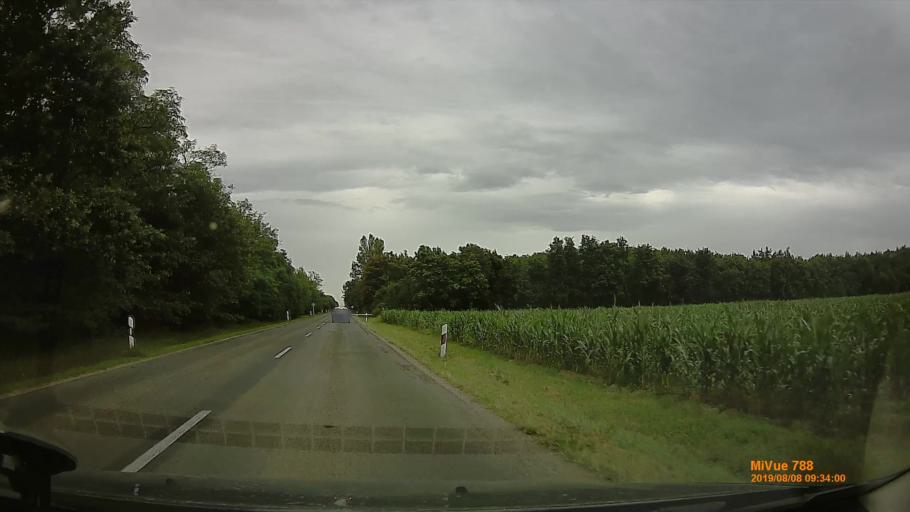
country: HU
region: Vas
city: Vasvar
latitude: 47.0287
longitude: 16.8155
